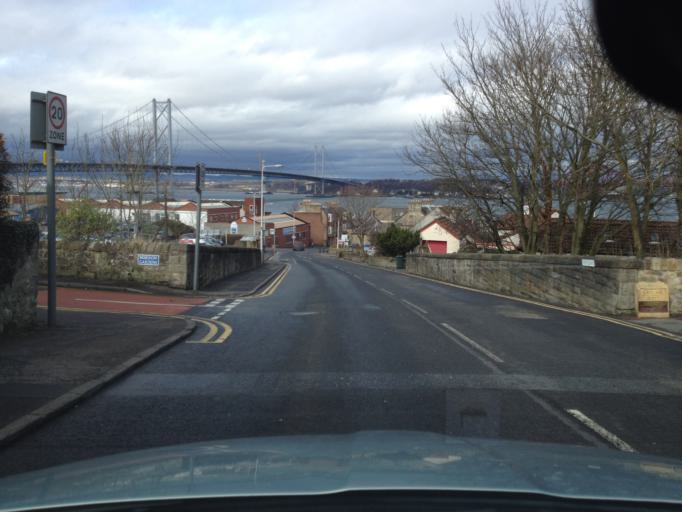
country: GB
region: Scotland
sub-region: Edinburgh
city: Queensferry
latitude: 55.9885
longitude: -3.3972
